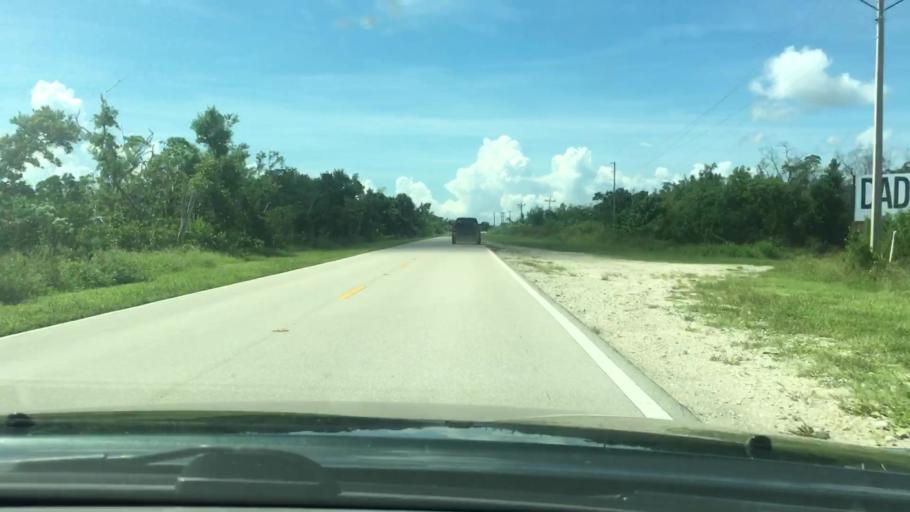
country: US
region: Florida
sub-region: Collier County
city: Marco
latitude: 25.9395
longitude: -81.6464
